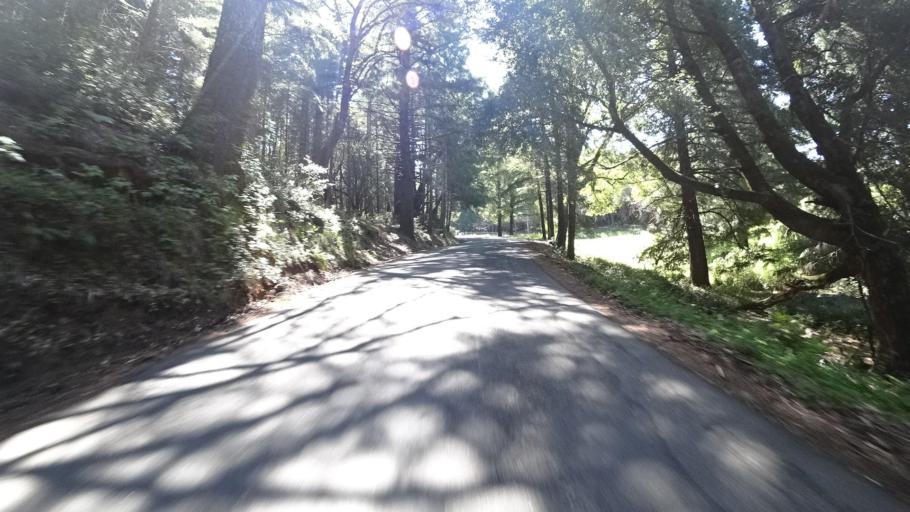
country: US
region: California
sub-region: Humboldt County
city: Redway
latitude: 40.1347
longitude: -123.9809
